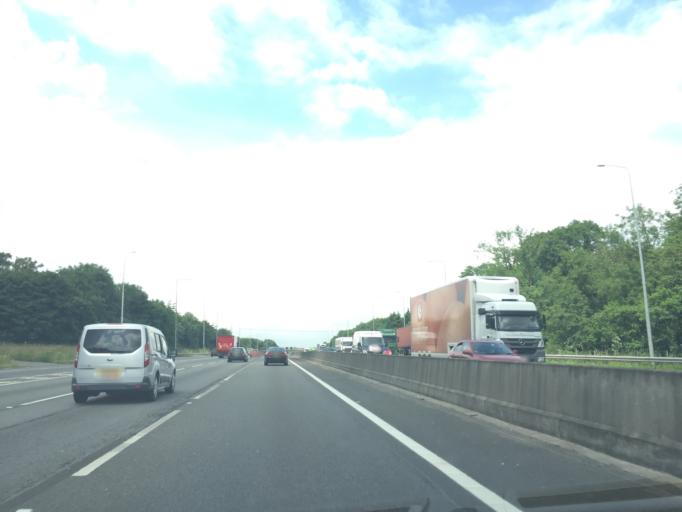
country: GB
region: England
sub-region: Buckinghamshire
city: Gerrards Cross
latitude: 51.5699
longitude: -0.5350
